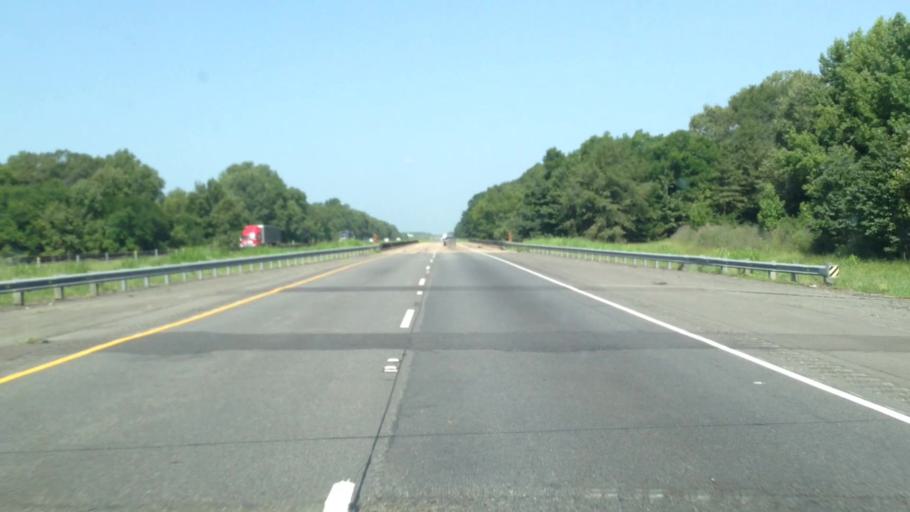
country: US
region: Louisiana
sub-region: Richland Parish
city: Delhi
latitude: 32.4348
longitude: -91.4408
